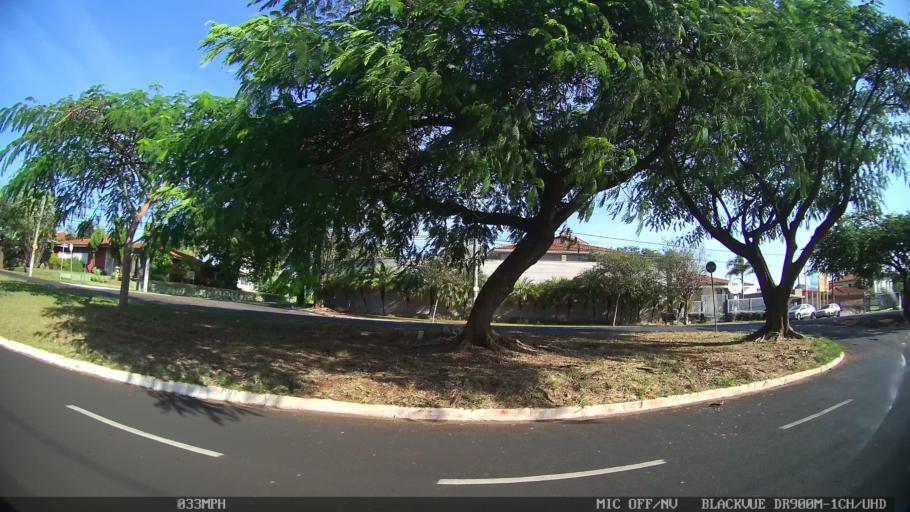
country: BR
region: Sao Paulo
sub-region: Ribeirao Preto
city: Ribeirao Preto
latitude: -21.2024
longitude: -47.7837
